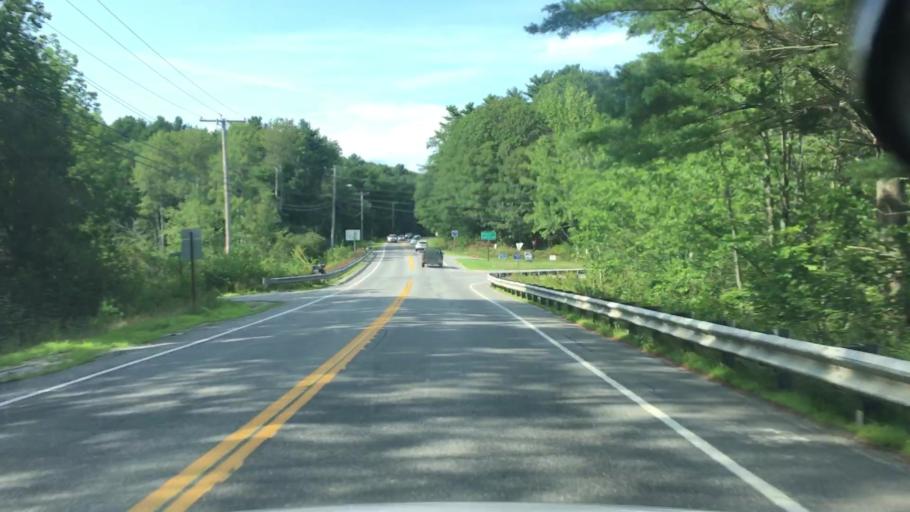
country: US
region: Maine
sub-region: Cumberland County
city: Brunswick
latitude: 43.8478
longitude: -69.9125
